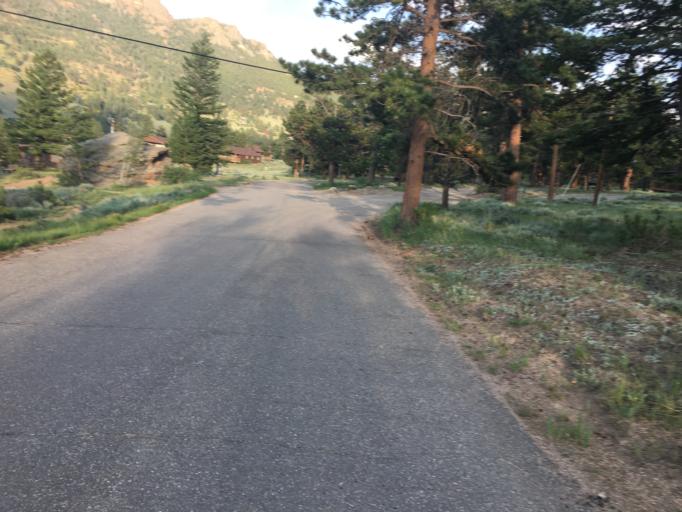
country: US
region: Colorado
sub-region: Larimer County
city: Estes Park
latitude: 40.3361
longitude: -105.5725
